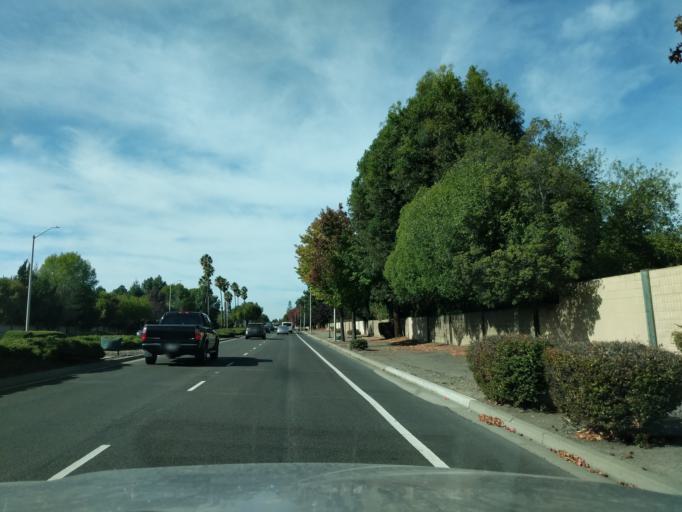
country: US
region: California
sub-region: Alameda County
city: Fremont
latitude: 37.5548
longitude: -121.9474
